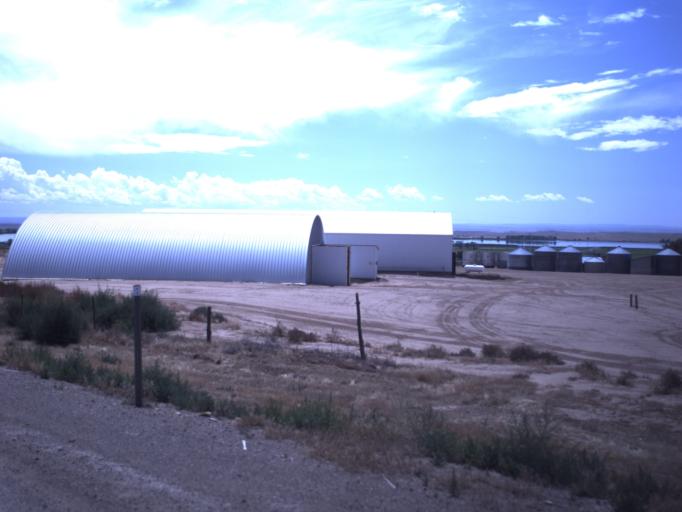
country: US
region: Utah
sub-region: Uintah County
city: Maeser
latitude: 40.2195
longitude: -109.6827
